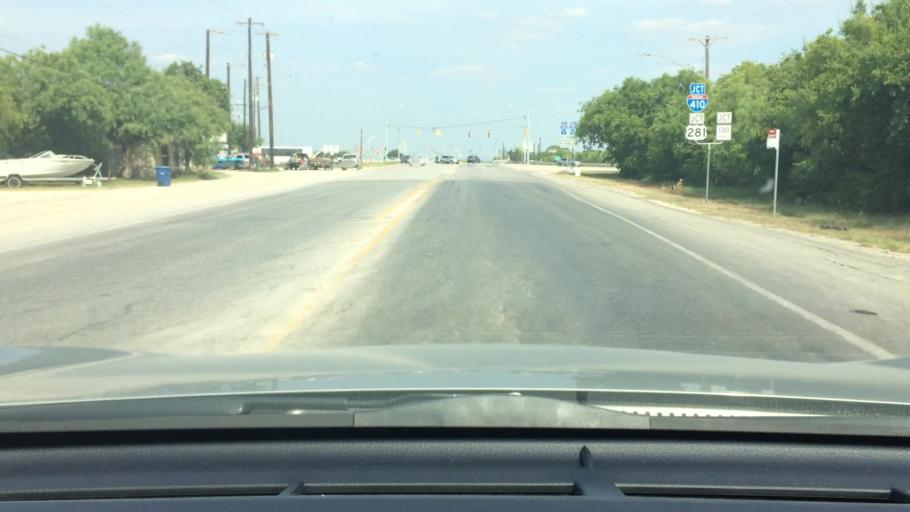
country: US
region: Texas
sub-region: Bexar County
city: China Grove
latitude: 29.3255
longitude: -98.4295
